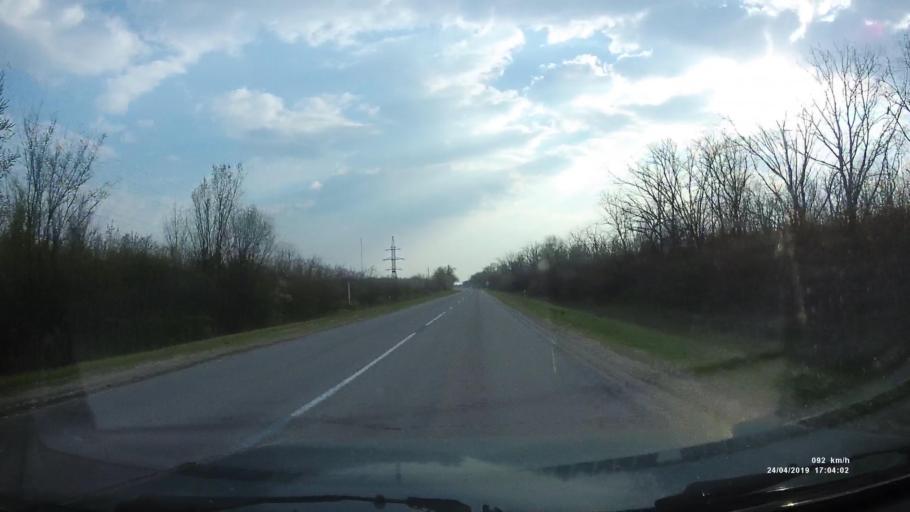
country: RU
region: Rostov
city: Sal'sk
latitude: 46.5605
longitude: 41.6034
